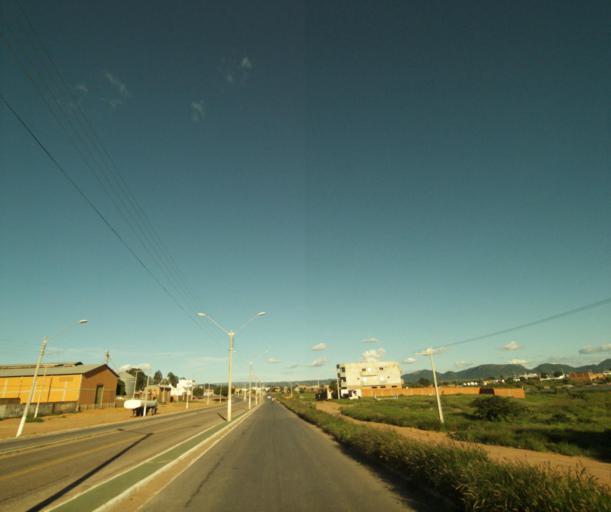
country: BR
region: Bahia
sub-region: Guanambi
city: Guanambi
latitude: -14.2092
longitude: -42.7683
